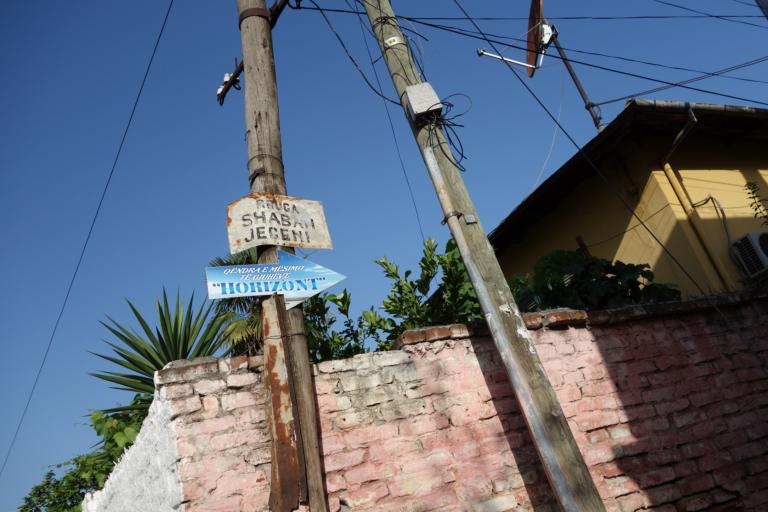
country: AL
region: Tirane
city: Tirana
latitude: 41.3340
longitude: 19.8317
